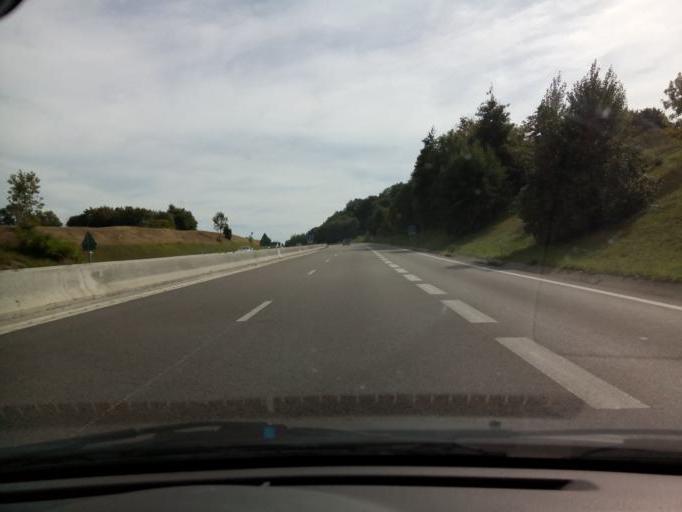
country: FR
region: Rhone-Alpes
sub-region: Departement de l'Isere
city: Chabons
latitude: 45.4590
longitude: 5.4016
